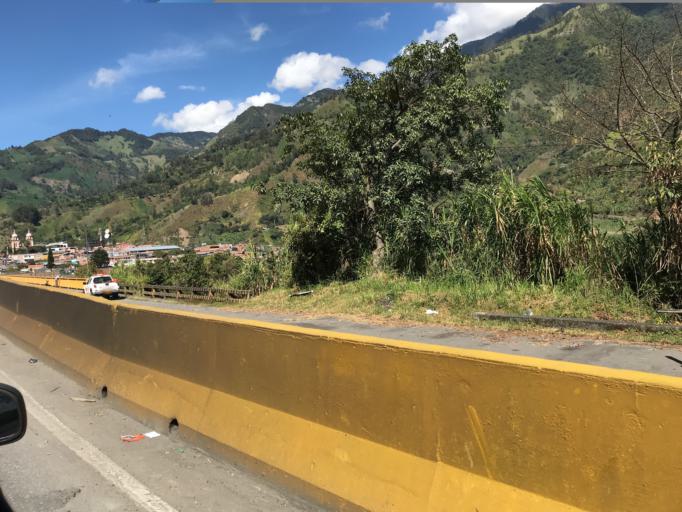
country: CO
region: Tolima
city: Cajamarca
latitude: 4.4415
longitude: -75.4214
